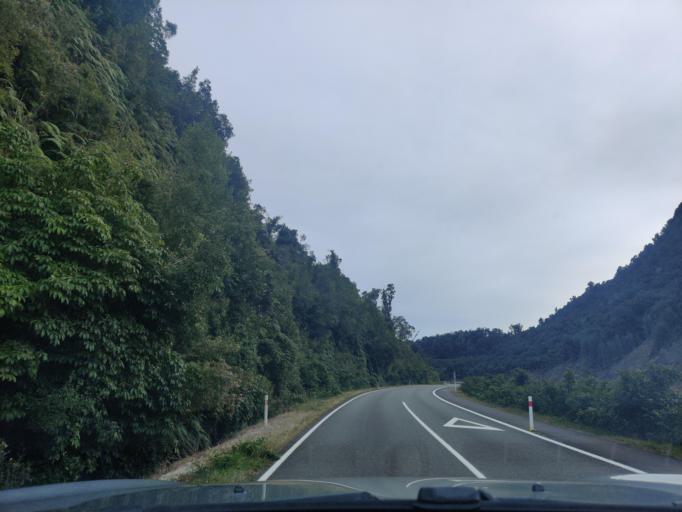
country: NZ
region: West Coast
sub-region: Westland District
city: Hokitika
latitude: -43.3994
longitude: 170.1805
